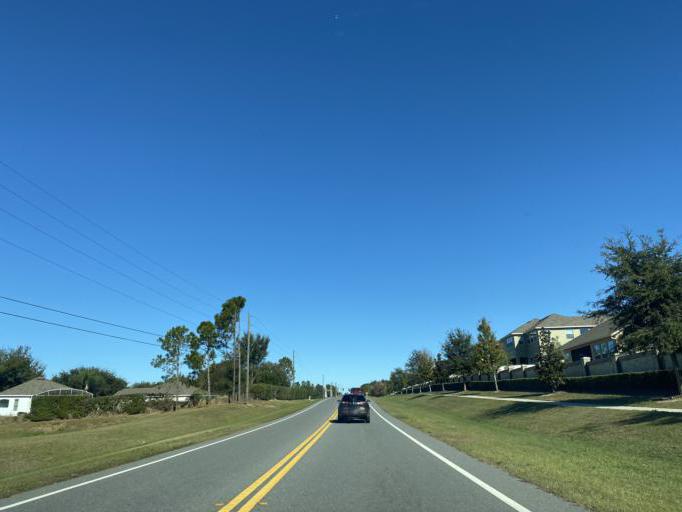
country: US
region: Florida
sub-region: Lake County
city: Clermont
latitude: 28.5035
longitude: -81.7071
